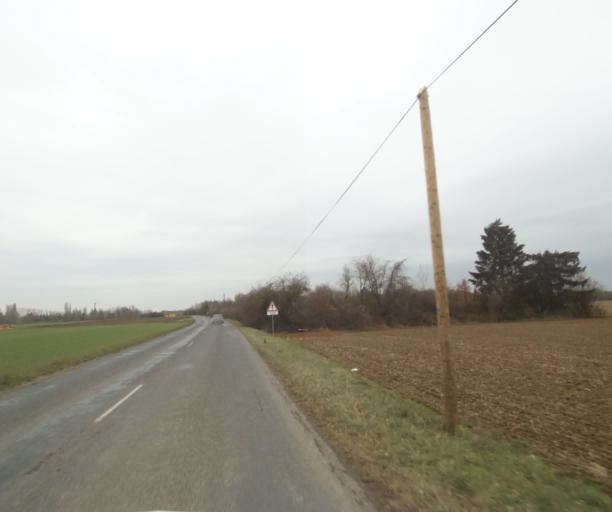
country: FR
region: Champagne-Ardenne
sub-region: Departement de la Haute-Marne
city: Villiers-en-Lieu
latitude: 48.6531
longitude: 4.9077
